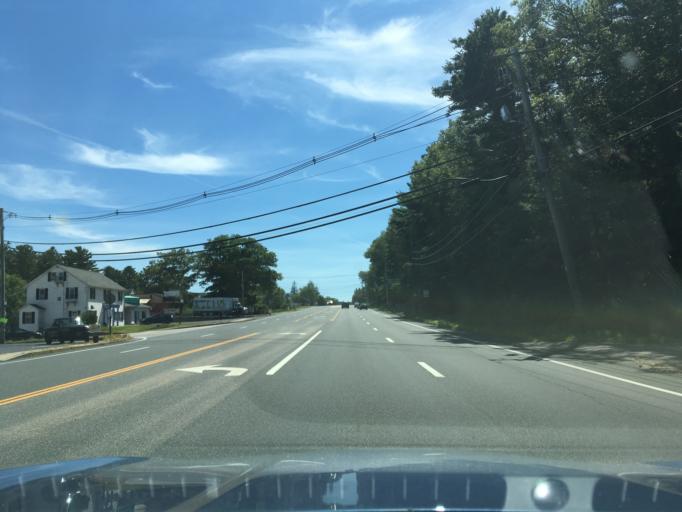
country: US
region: Rhode Island
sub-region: Kent County
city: West Greenwich
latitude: 41.6604
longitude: -71.6029
